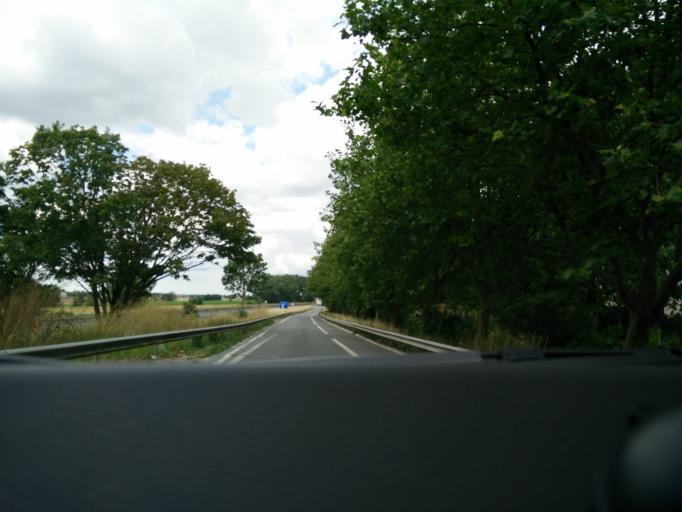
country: FR
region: Nord-Pas-de-Calais
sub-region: Departement du Nord
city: Steenvoorde
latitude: 50.8102
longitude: 2.5983
